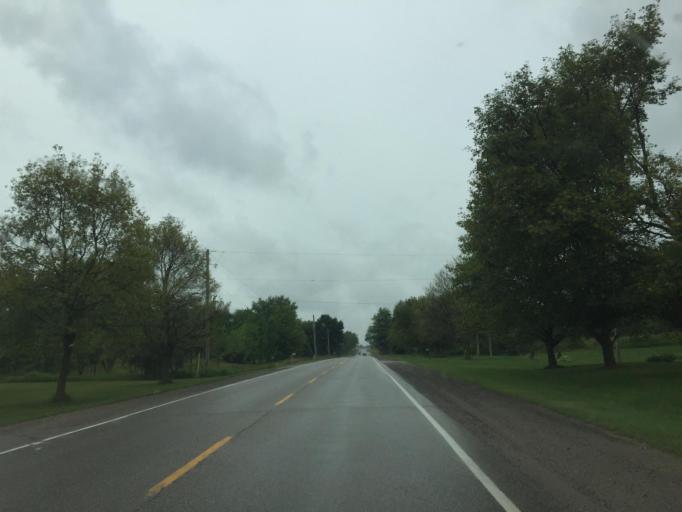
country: CA
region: Ontario
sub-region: Wellington County
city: Guelph
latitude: 43.4497
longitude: -80.2256
